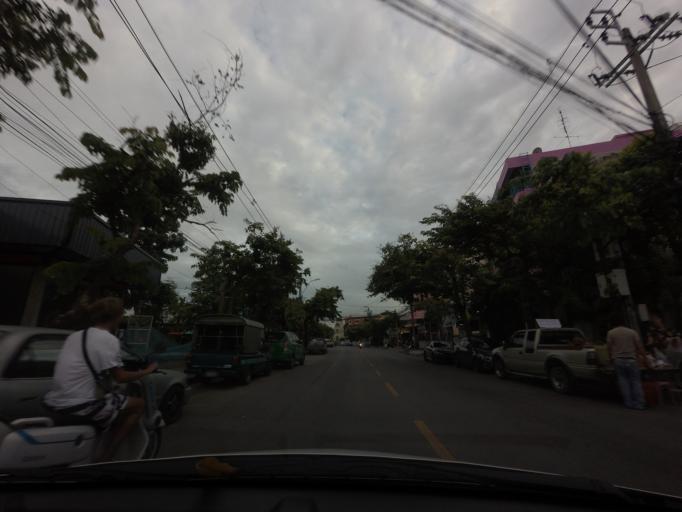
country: TH
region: Bangkok
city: Chom Thong
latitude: 13.6898
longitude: 100.4637
